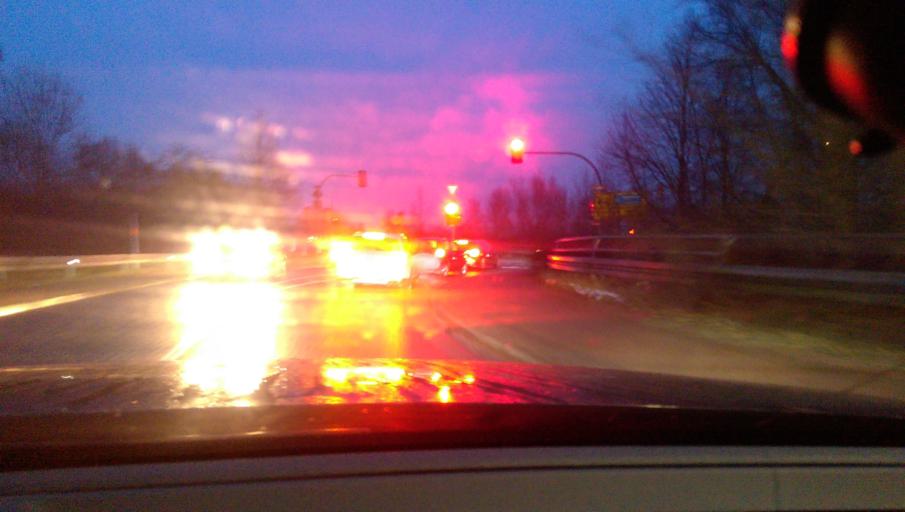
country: DE
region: Lower Saxony
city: Gross Munzel
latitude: 52.4067
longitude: 9.5175
